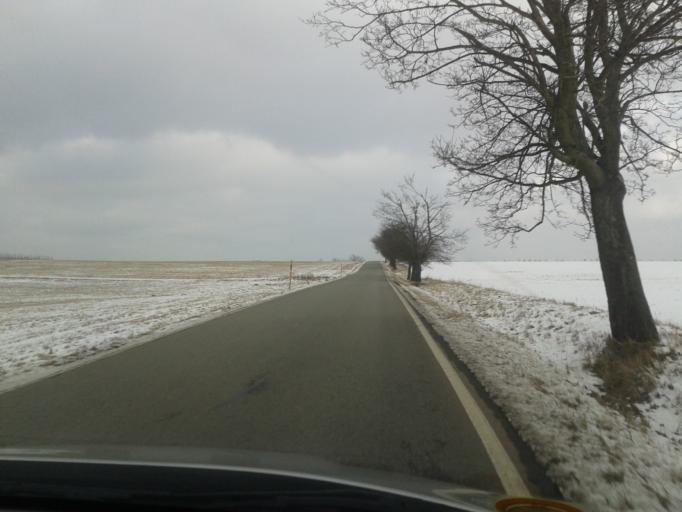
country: CZ
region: Olomoucky
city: Horni Stepanov
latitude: 49.5776
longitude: 16.8279
